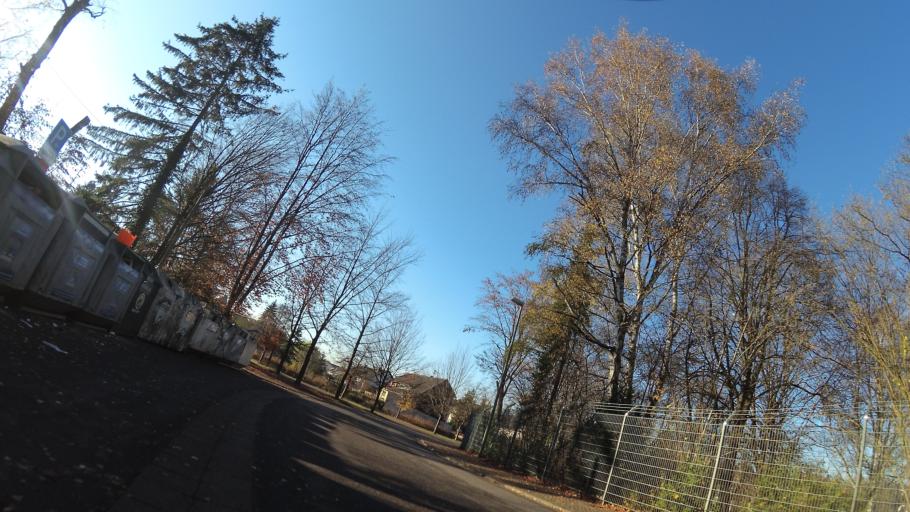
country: DE
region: Saarland
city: Schwalbach
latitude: 49.2949
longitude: 6.8091
